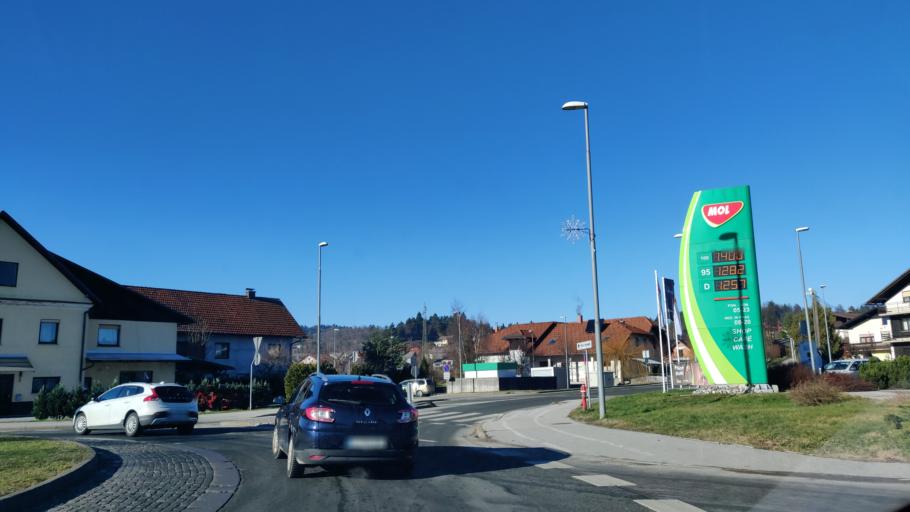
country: SI
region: Logatec
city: Logatec
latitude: 45.9164
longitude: 14.2188
